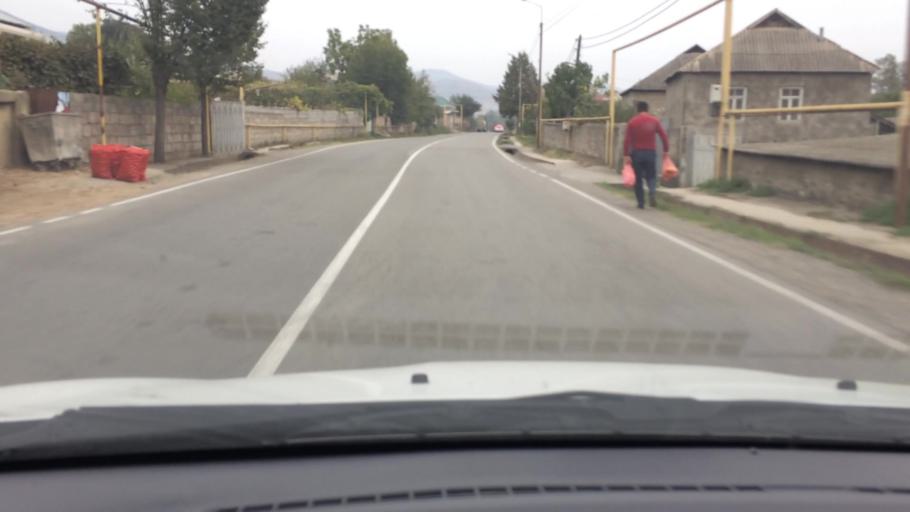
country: AM
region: Tavush
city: Bagratashen
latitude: 41.2412
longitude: 44.7999
